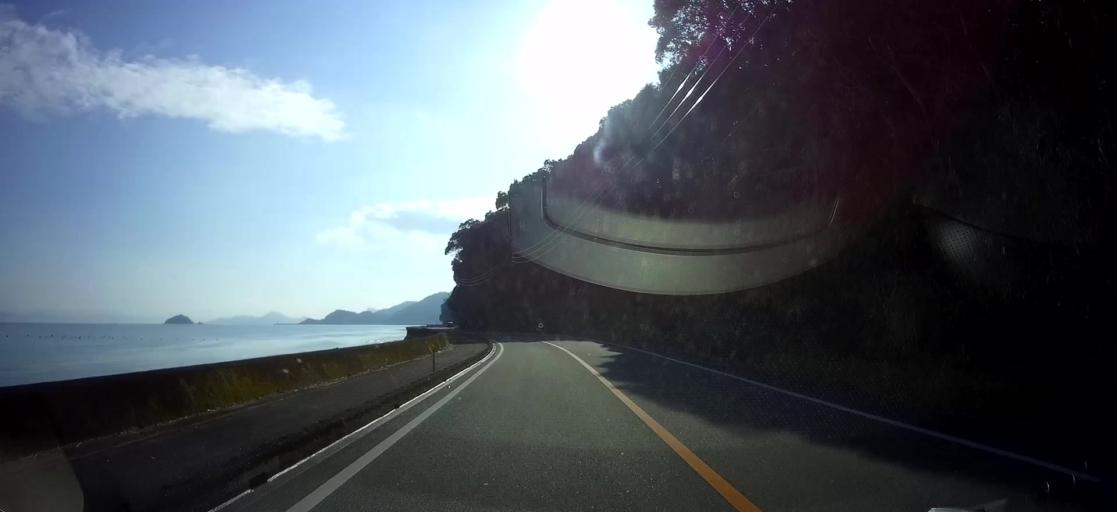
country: JP
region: Kumamoto
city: Yatsushiro
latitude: 32.4969
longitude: 130.4452
